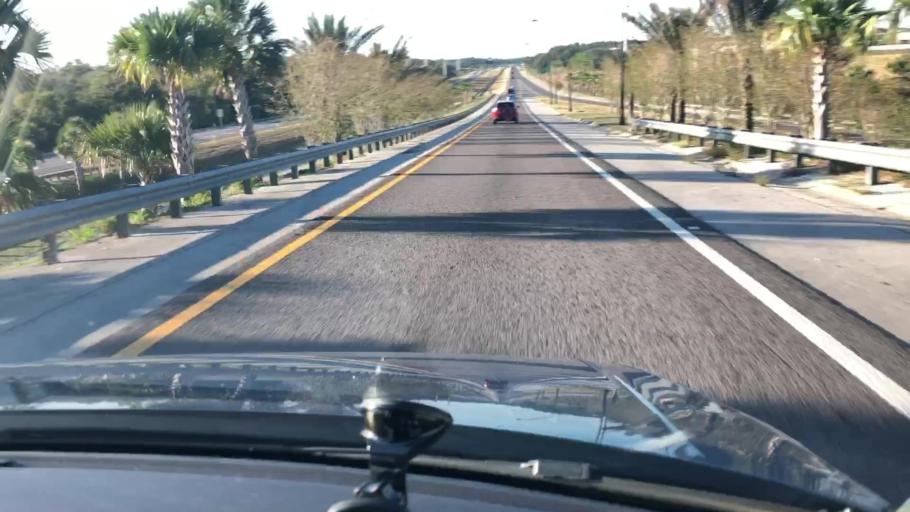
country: US
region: Florida
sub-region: Polk County
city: Loughman
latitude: 28.2849
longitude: -81.5945
